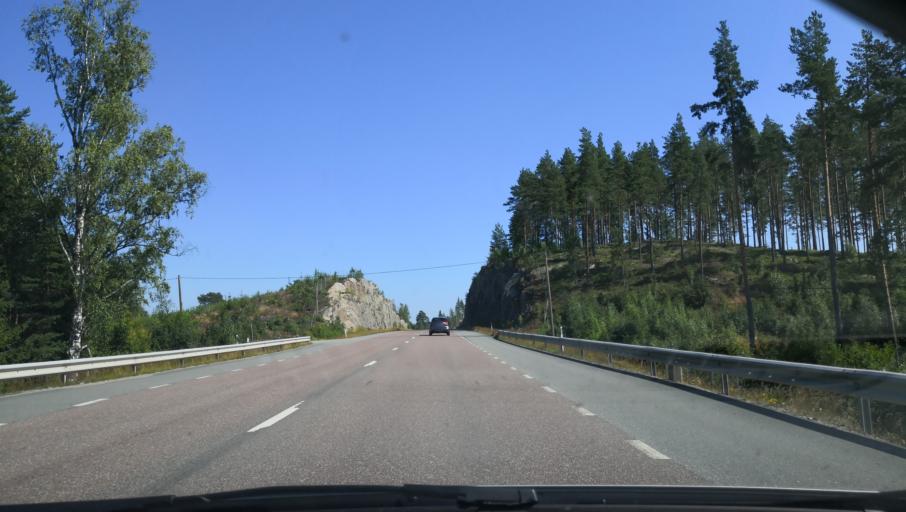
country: SE
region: Gaevleborg
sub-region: Bollnas Kommun
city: Bollnas
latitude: 61.3294
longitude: 16.2525
